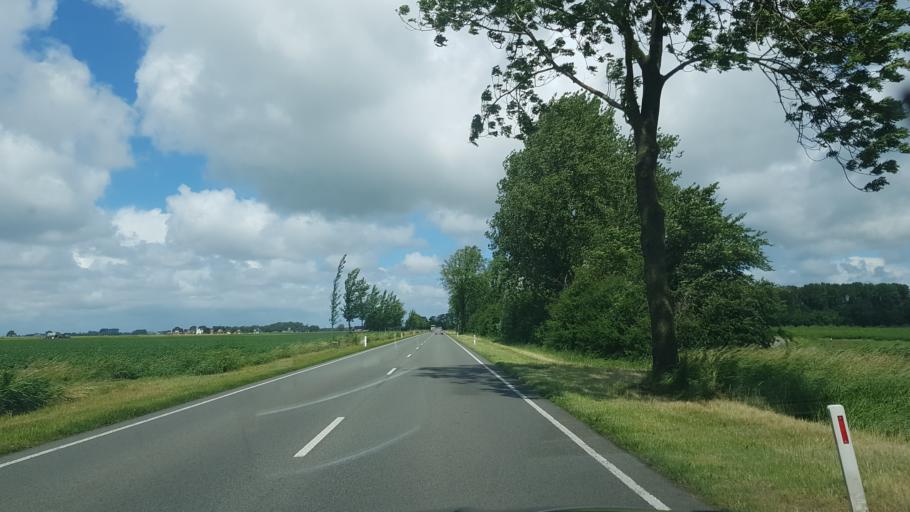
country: NL
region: Groningen
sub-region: Gemeente Winsum
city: Winsum
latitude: 53.3552
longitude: 6.5073
